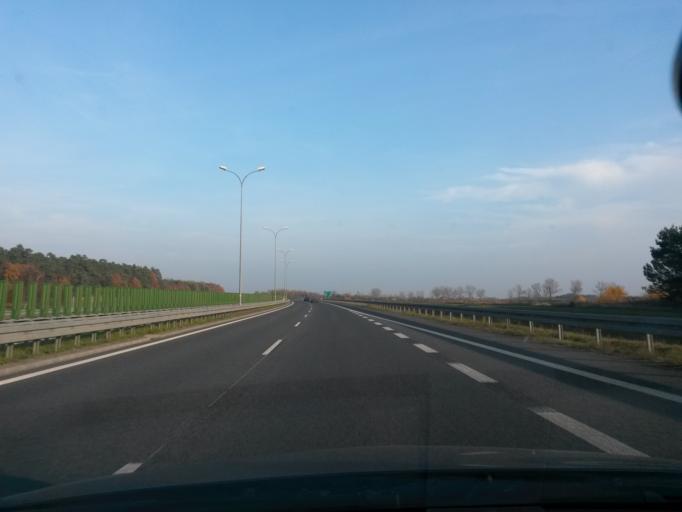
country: PL
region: Lower Silesian Voivodeship
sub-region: Powiat olesnicki
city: Olesnica
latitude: 51.2261
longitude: 17.4498
